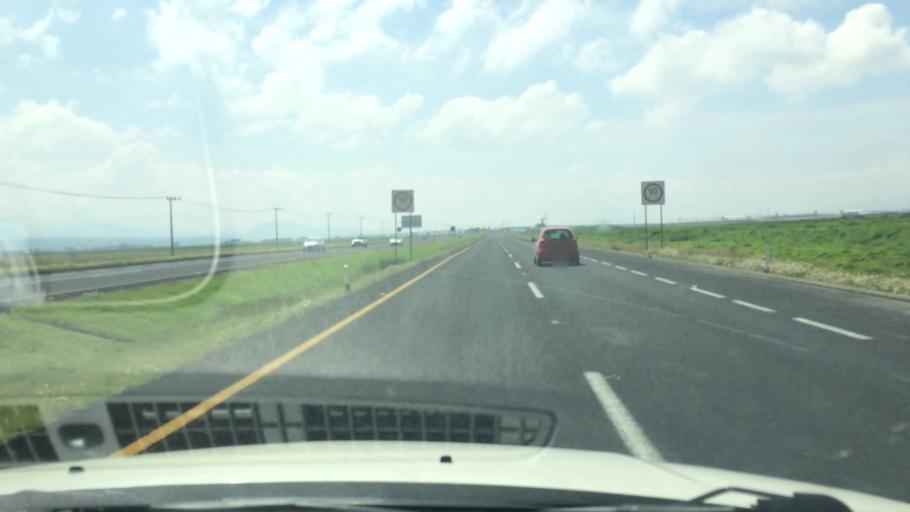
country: MX
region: Mexico
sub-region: Toluca
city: El Cerrillo Vista Hermosa
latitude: 19.3392
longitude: -99.5281
